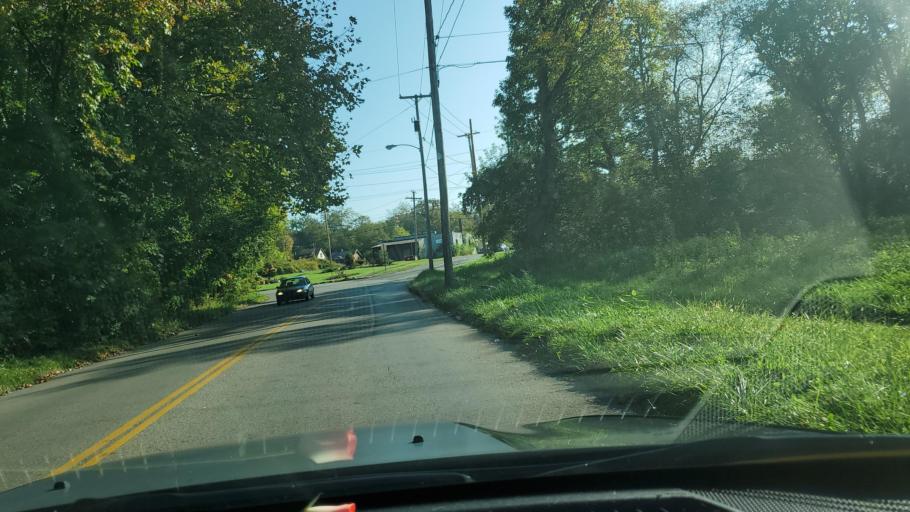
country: US
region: Ohio
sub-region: Mahoning County
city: Youngstown
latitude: 41.1225
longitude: -80.6329
